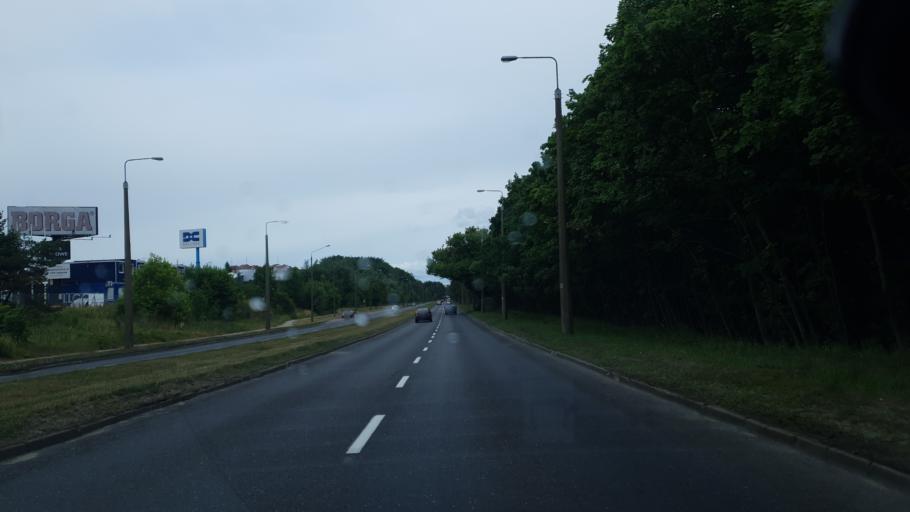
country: PL
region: Pomeranian Voivodeship
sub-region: Gdynia
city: Wielki Kack
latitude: 54.4630
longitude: 18.4617
